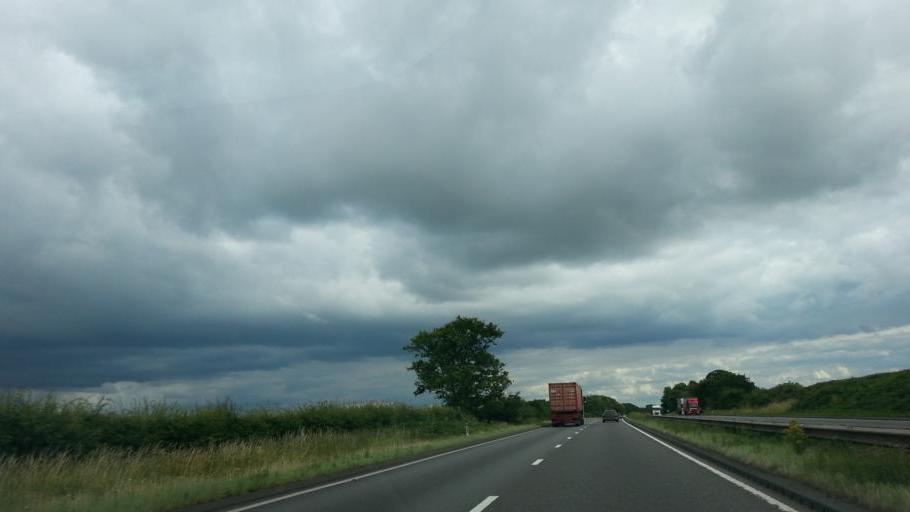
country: GB
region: England
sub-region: Nottinghamshire
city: Bircotes
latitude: 53.3573
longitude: -1.0427
